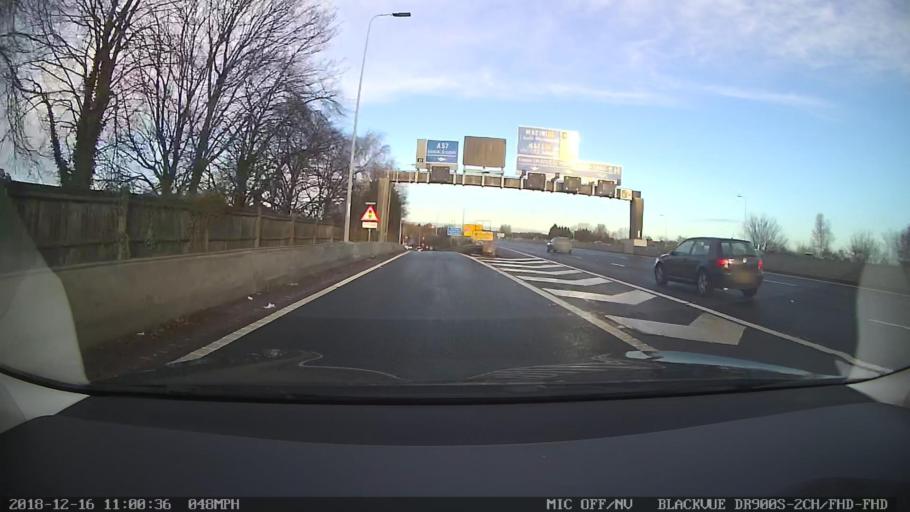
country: GB
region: England
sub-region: Trafford
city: Urmston
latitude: 53.4744
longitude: -2.3729
